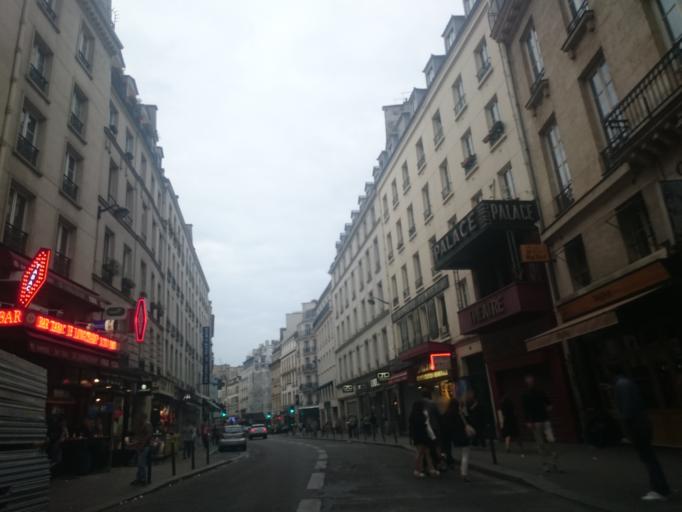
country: FR
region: Ile-de-France
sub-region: Paris
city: Paris
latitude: 48.8720
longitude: 2.3431
